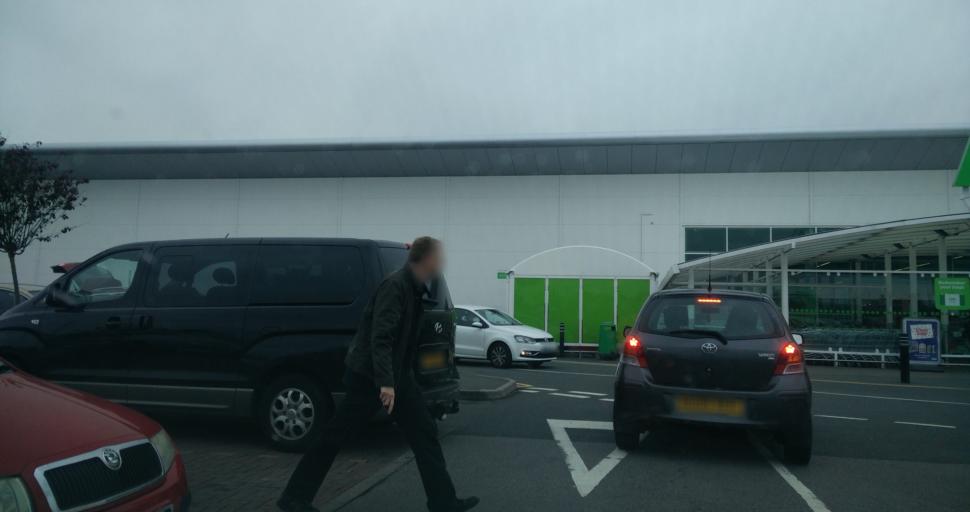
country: GB
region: England
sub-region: County Durham
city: Bishop Auckland
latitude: 54.6581
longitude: -1.6729
